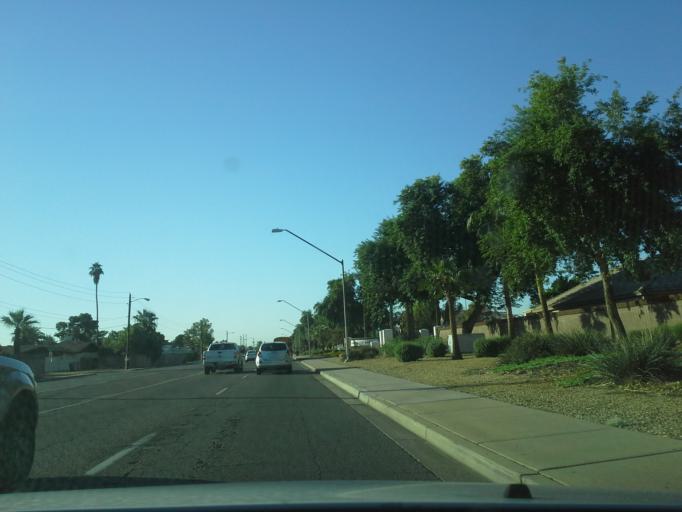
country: US
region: Arizona
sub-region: Maricopa County
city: Glendale
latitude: 33.5495
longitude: -112.1688
